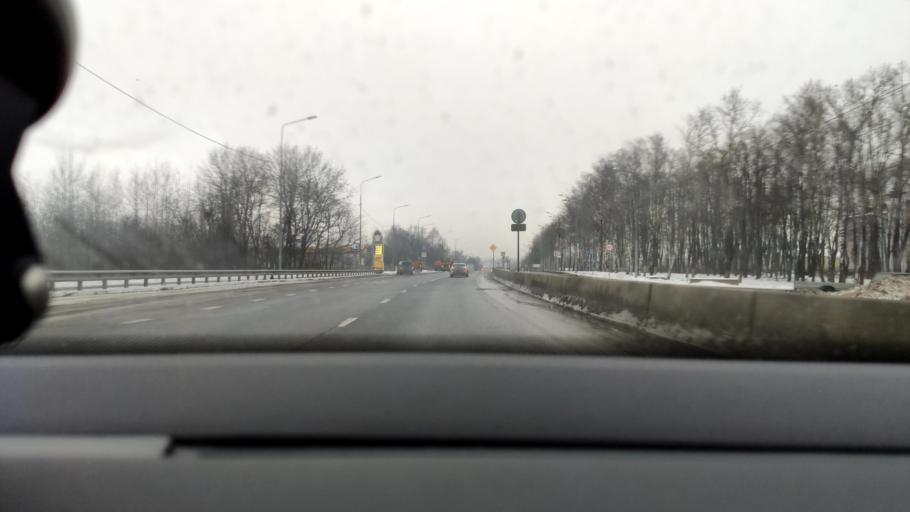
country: RU
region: Moskovskaya
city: Sergiyev Posad
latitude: 56.2729
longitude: 38.1210
